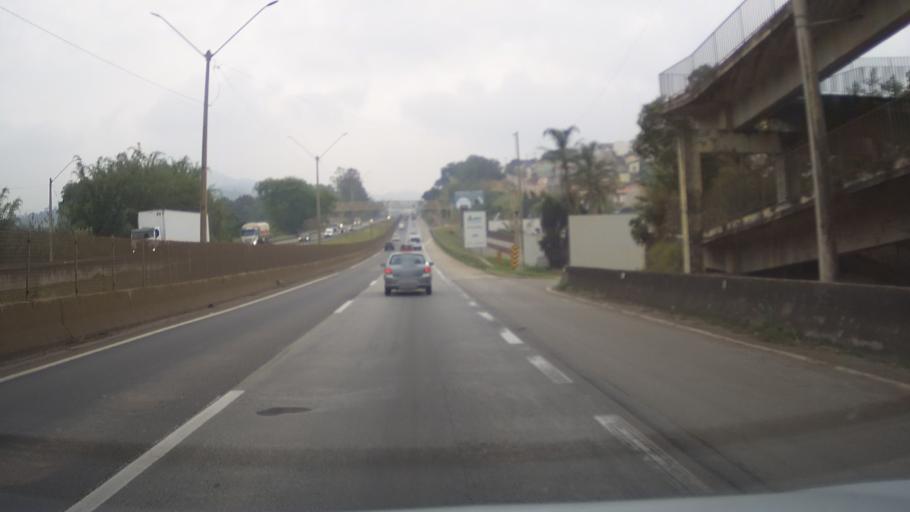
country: BR
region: Sao Paulo
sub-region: Atibaia
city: Atibaia
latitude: -23.0535
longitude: -46.5683
